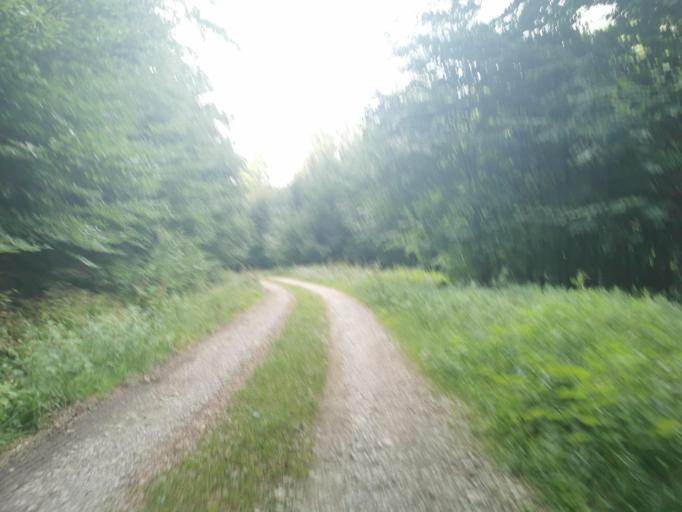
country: SK
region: Trenciansky
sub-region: Okres Myjava
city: Myjava
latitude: 48.8217
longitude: 17.5948
